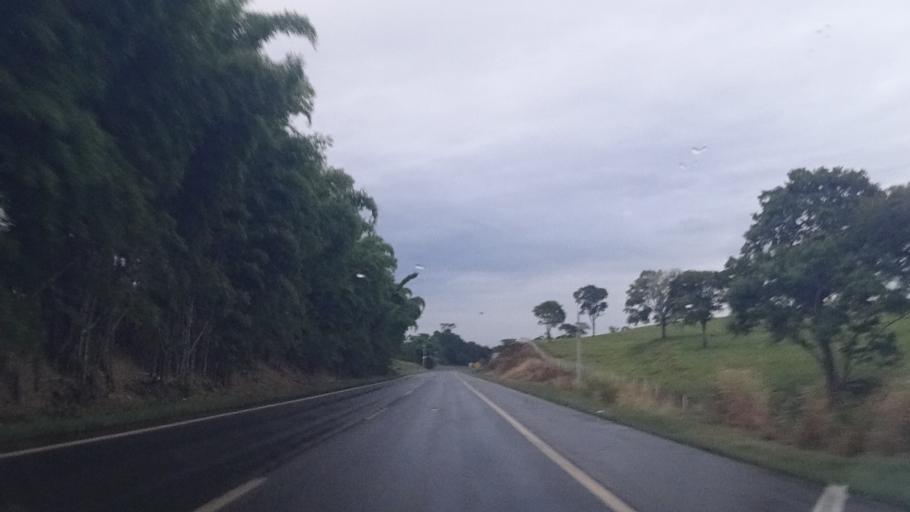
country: BR
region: Goias
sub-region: Goianapolis
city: Goianapolis
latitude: -16.4502
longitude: -49.0335
